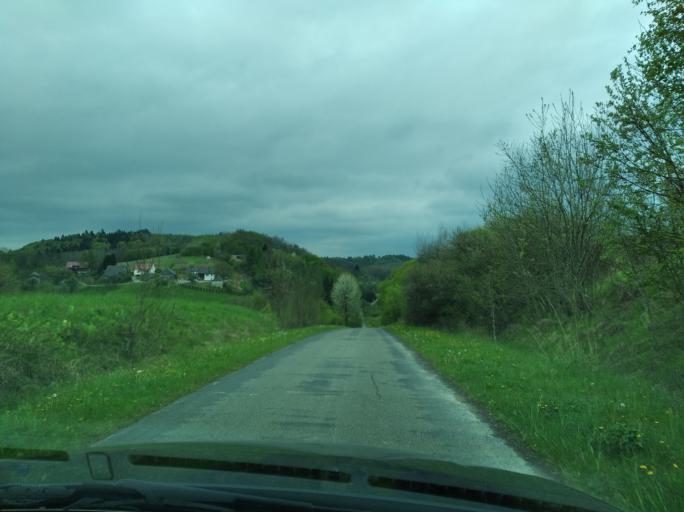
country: PL
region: Subcarpathian Voivodeship
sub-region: Powiat brzozowski
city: Dydnia
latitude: 49.6645
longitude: 22.2556
